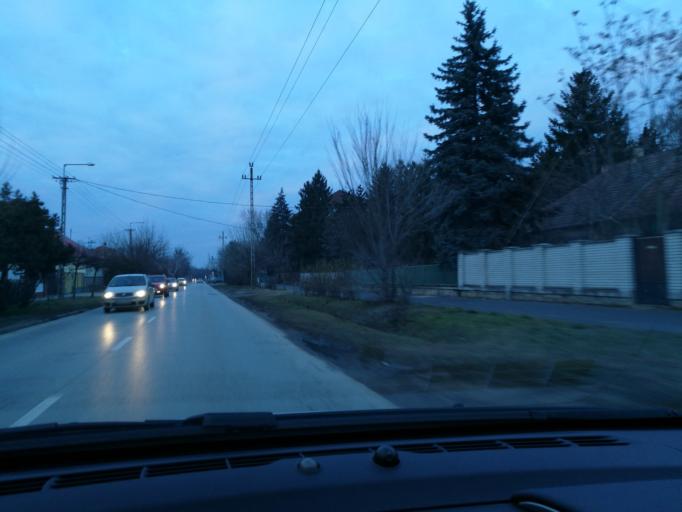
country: HU
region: Szabolcs-Szatmar-Bereg
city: Nyiregyhaza
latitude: 47.9734
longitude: 21.7070
